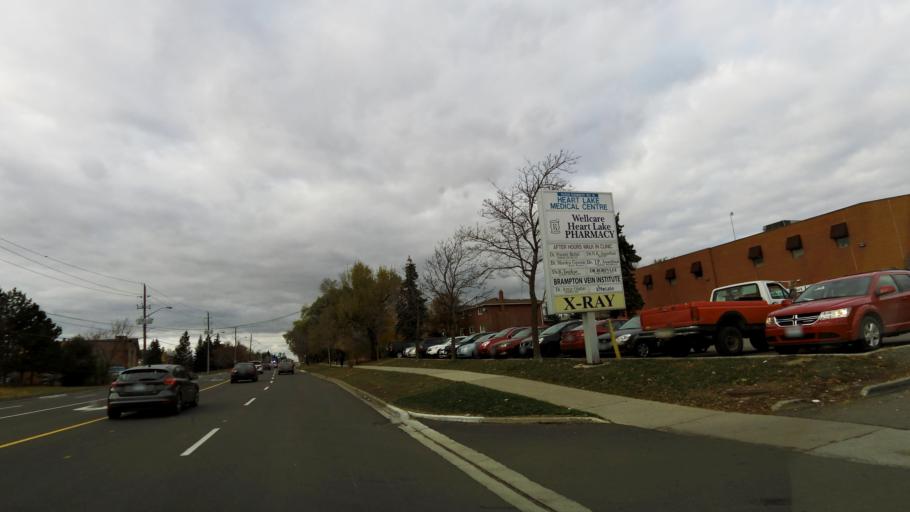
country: CA
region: Ontario
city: Brampton
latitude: 43.7241
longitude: -79.7877
